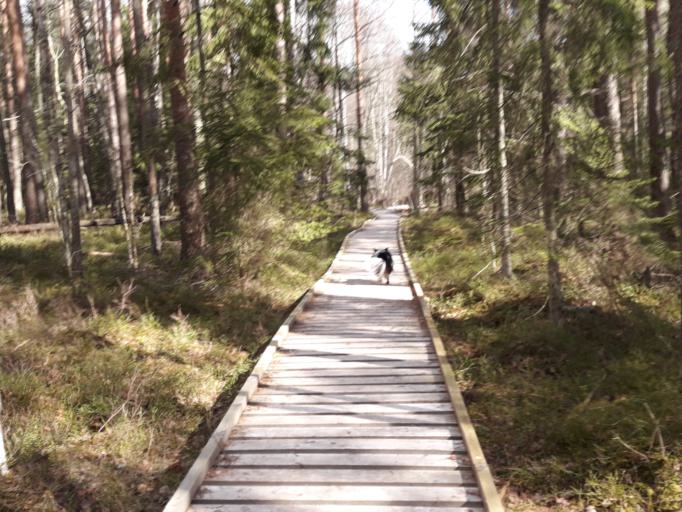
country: LV
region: Talsu Rajons
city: Sabile
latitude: 56.9073
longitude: 22.3955
